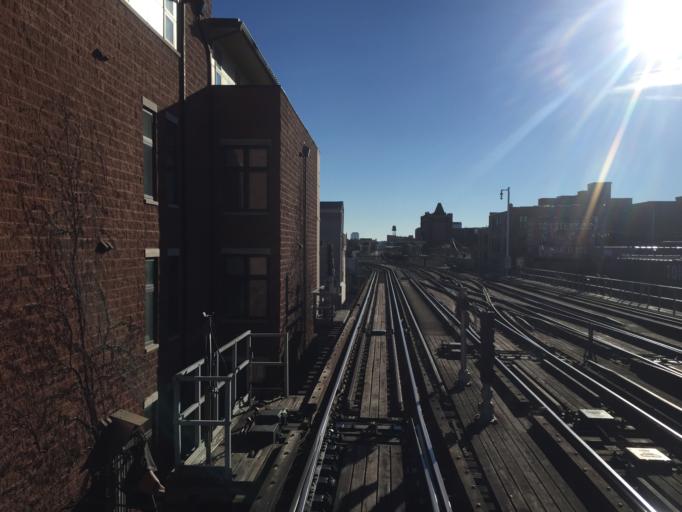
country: US
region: Illinois
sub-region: Cook County
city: Chicago
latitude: 41.9415
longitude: -87.6534
